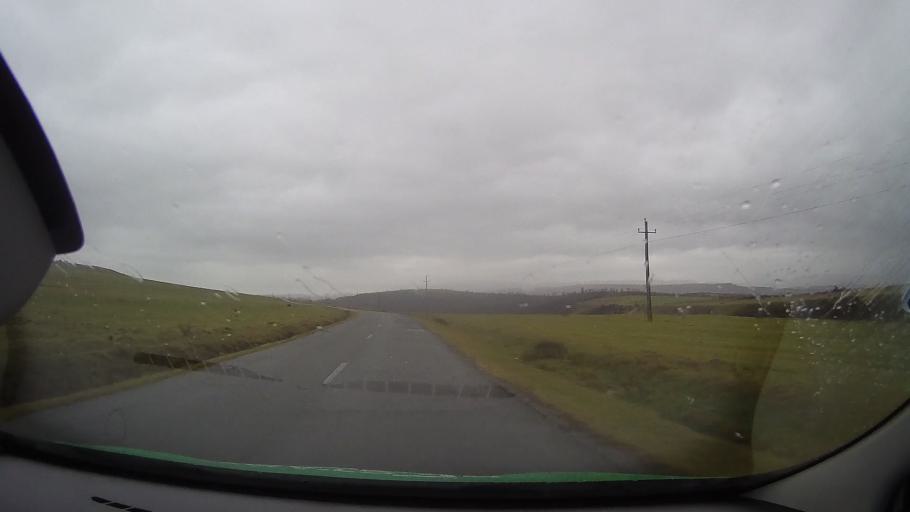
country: RO
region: Mures
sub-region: Comuna Brancovenesti
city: Valenii de Mures
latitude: 46.9088
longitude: 24.7838
